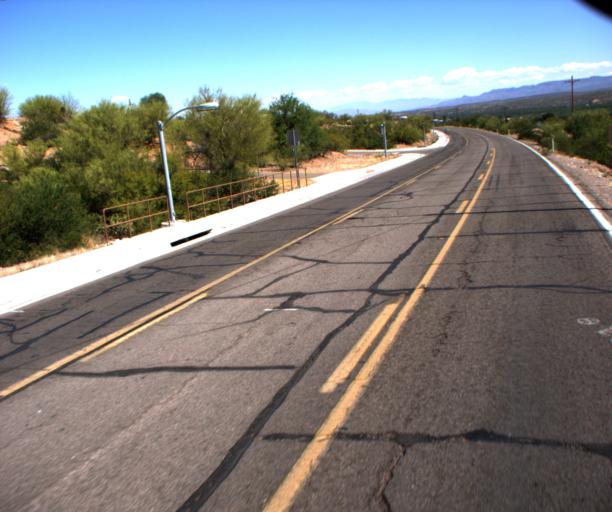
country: US
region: Arizona
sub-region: Pinal County
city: Mammoth
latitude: 32.7126
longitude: -110.6414
